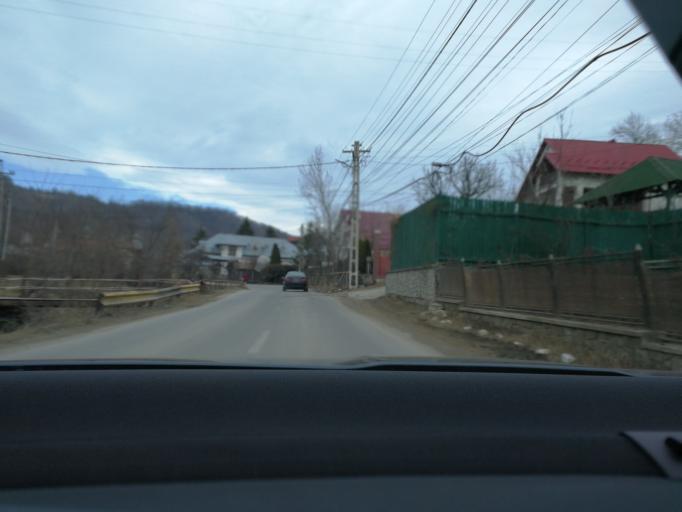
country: RO
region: Prahova
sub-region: Comuna Telega
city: Telega
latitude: 45.1369
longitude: 25.7867
